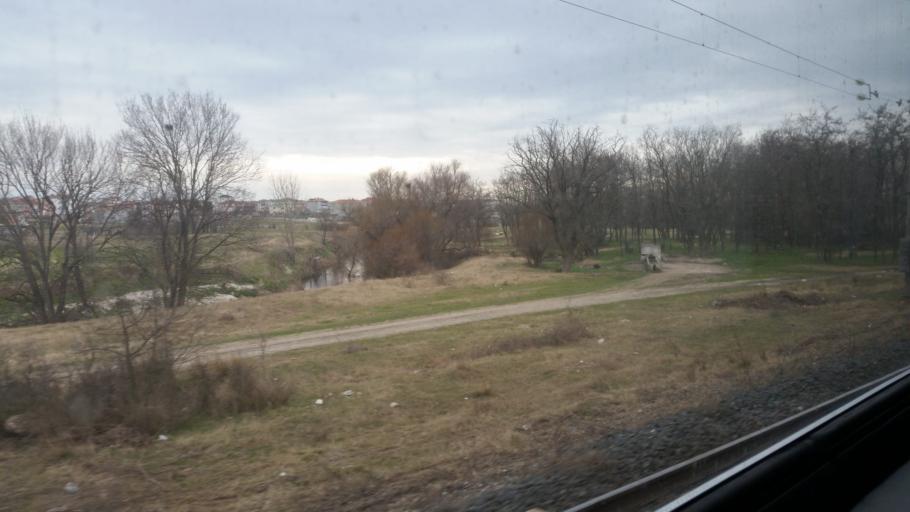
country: TR
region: Tekirdag
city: Velimese
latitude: 41.2499
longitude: 27.8893
